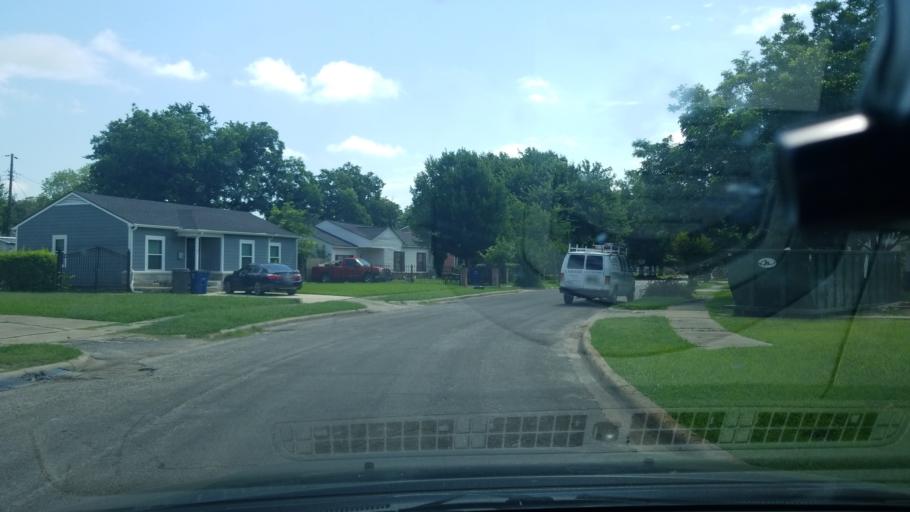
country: US
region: Texas
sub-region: Dallas County
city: Balch Springs
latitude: 32.7361
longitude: -96.6894
